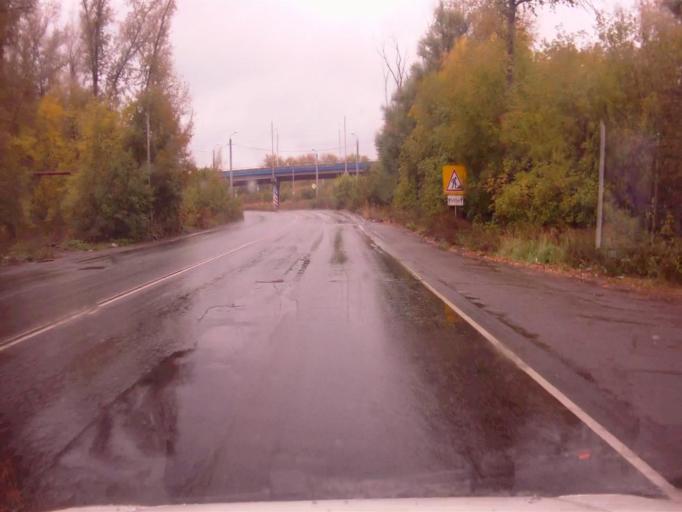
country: RU
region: Chelyabinsk
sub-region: Gorod Chelyabinsk
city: Chelyabinsk
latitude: 55.1972
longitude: 61.3893
